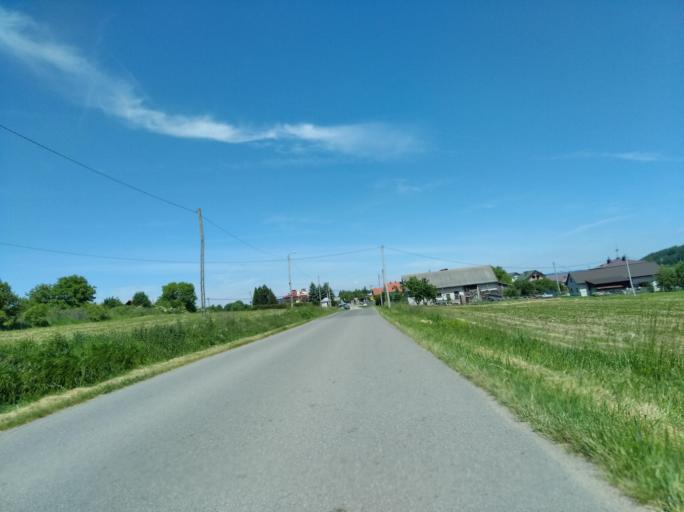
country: PL
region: Subcarpathian Voivodeship
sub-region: Powiat jasielski
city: Osiek Jasielski
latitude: 49.6702
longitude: 21.5437
